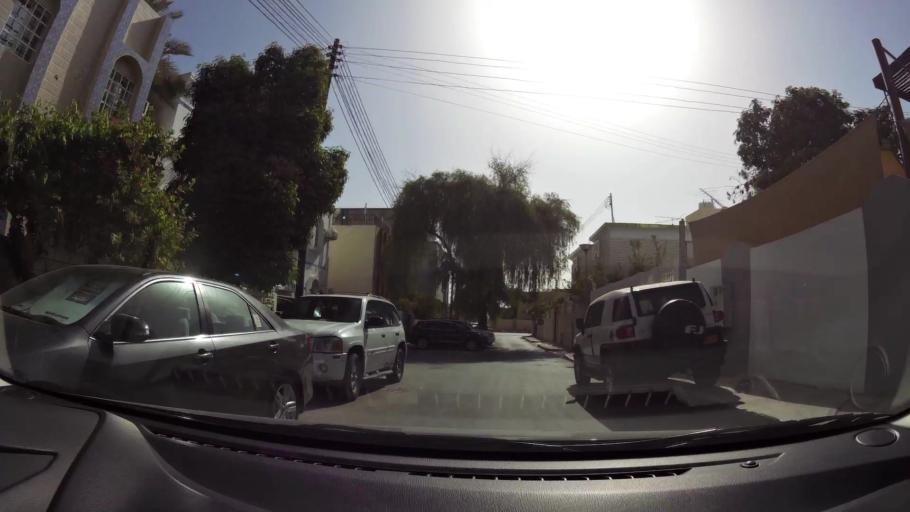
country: OM
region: Muhafazat Masqat
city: Muscat
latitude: 23.6034
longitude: 58.5119
